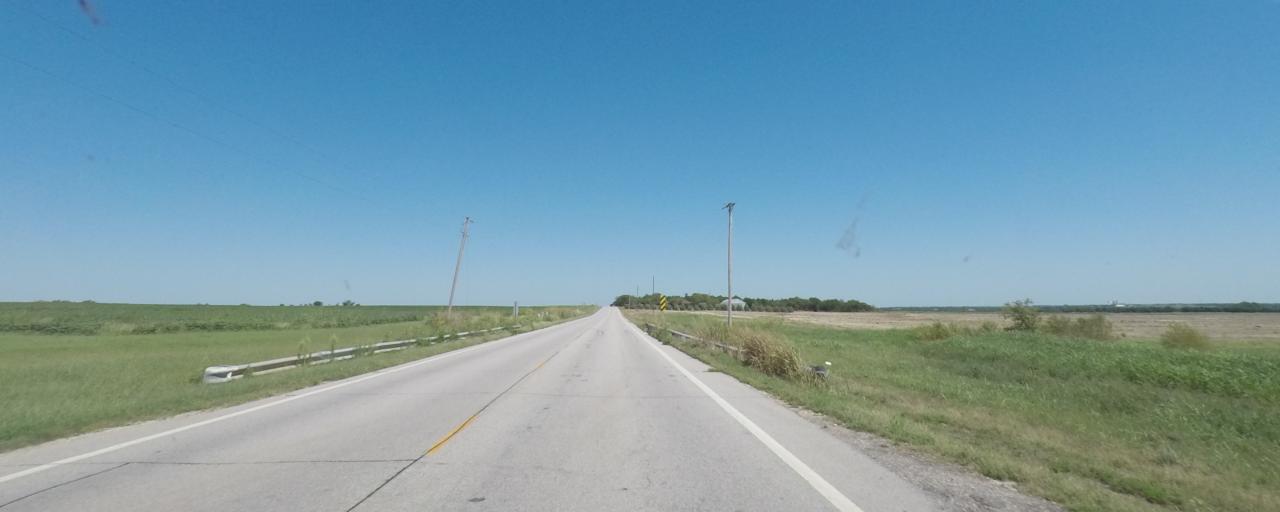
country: US
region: Kansas
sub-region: Sumner County
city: Wellington
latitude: 37.2125
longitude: -97.4023
